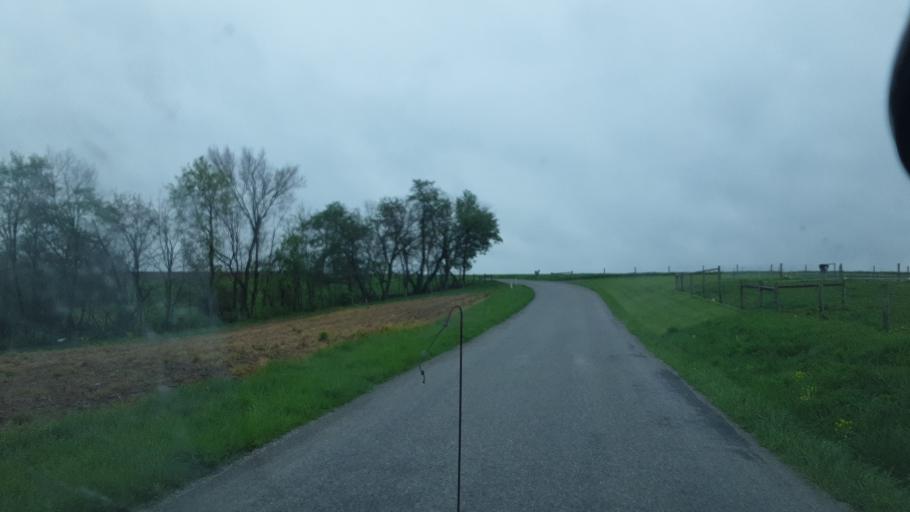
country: US
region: Ohio
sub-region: Holmes County
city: Millersburg
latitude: 40.6021
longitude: -81.8736
